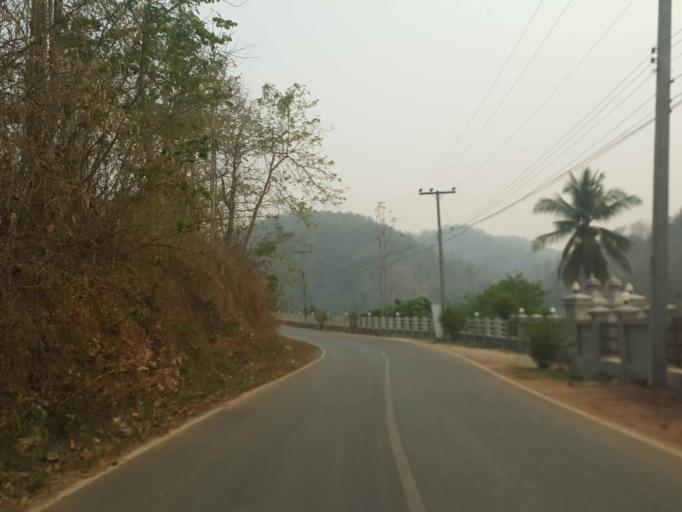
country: TH
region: Chiang Mai
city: Mae Taeng
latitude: 19.1288
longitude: 98.8837
